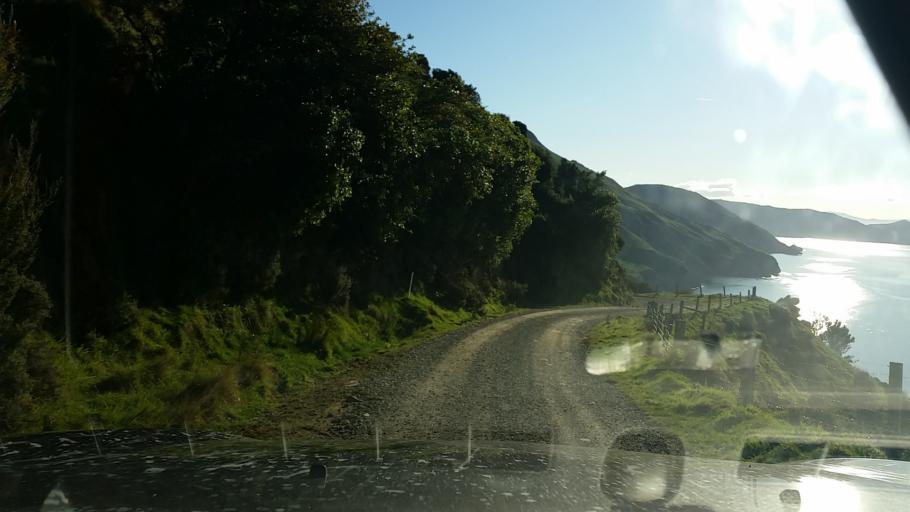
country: NZ
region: Marlborough
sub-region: Marlborough District
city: Picton
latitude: -41.0243
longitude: 174.1470
